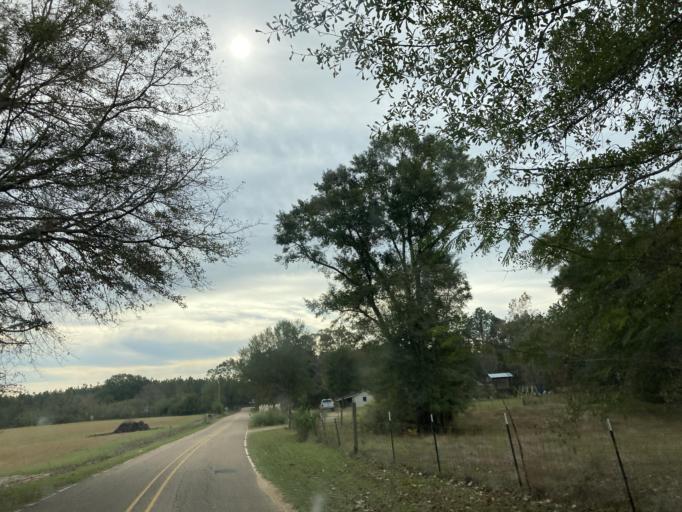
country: US
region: Mississippi
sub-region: Lamar County
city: Purvis
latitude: 31.0960
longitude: -89.4674
